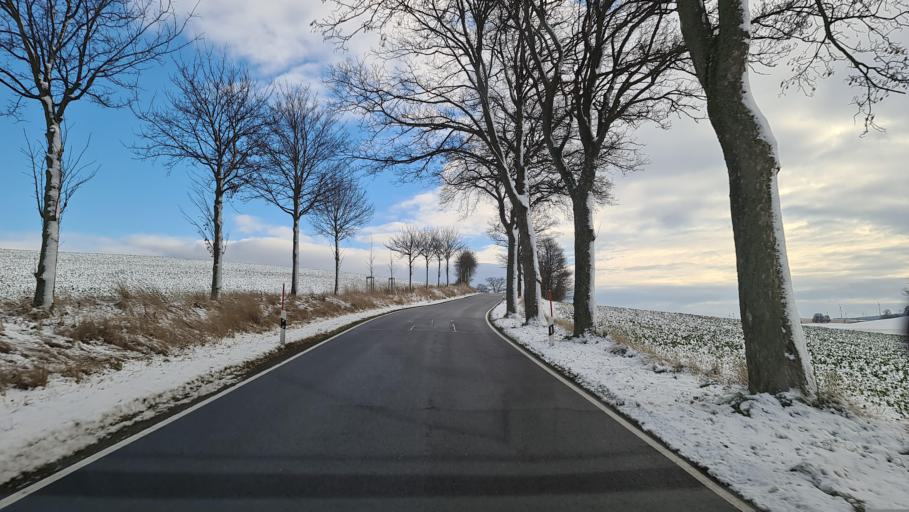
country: DE
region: Saxony
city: Grosshartmannsdorf
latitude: 50.7937
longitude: 13.3046
